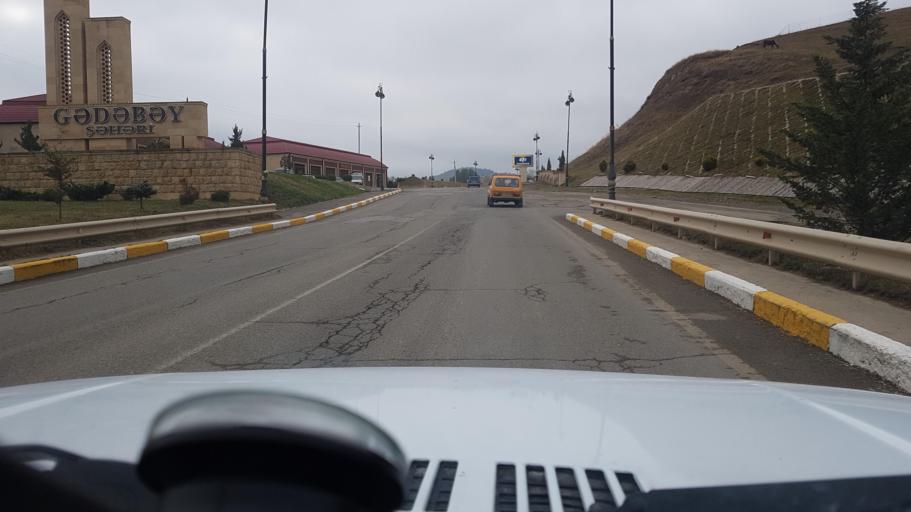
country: AZ
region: Gadabay Rayon
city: Ariqdam
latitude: 40.5853
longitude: 45.8109
